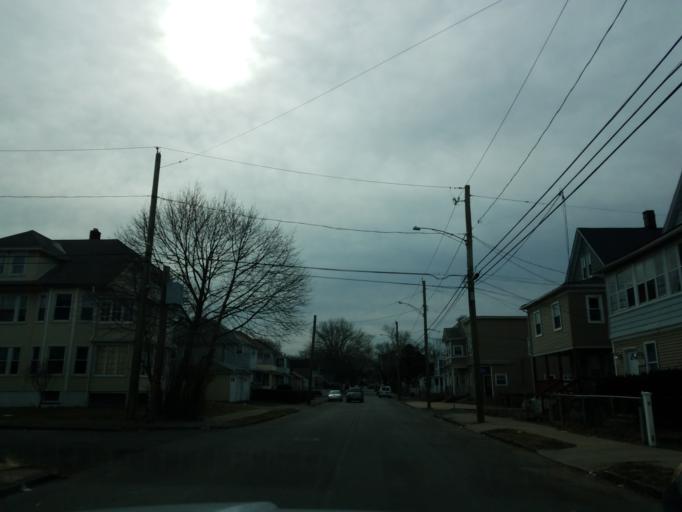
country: US
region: Connecticut
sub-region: Fairfield County
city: Bridgeport
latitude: 41.1840
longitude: -73.2104
